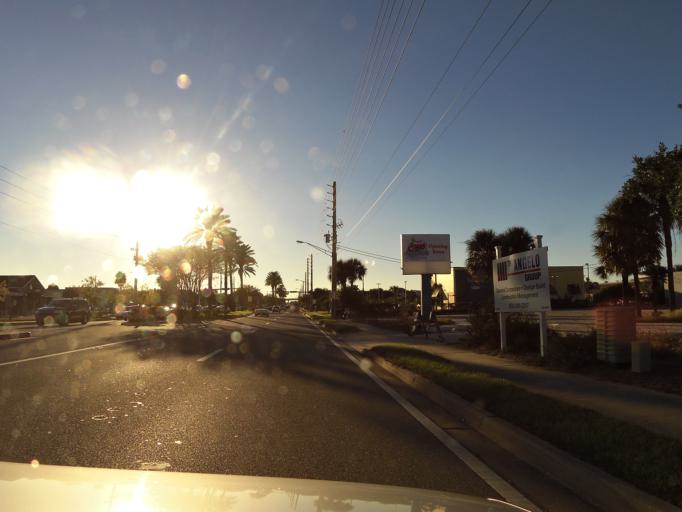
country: US
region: Florida
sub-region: Duval County
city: Atlantic Beach
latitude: 30.3246
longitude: -81.4099
